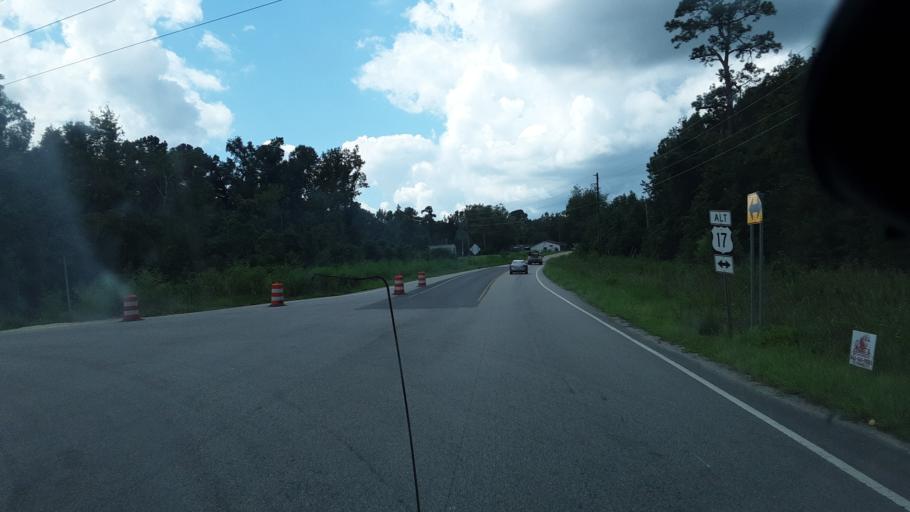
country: US
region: South Carolina
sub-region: Williamsburg County
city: Andrews
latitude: 33.3691
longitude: -79.4509
